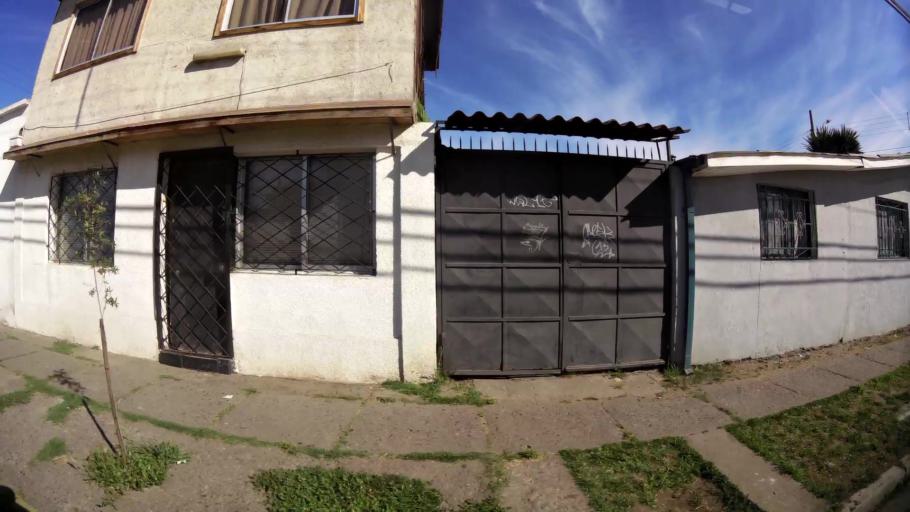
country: CL
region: Santiago Metropolitan
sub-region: Provincia de Santiago
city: Lo Prado
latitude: -33.4642
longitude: -70.7071
